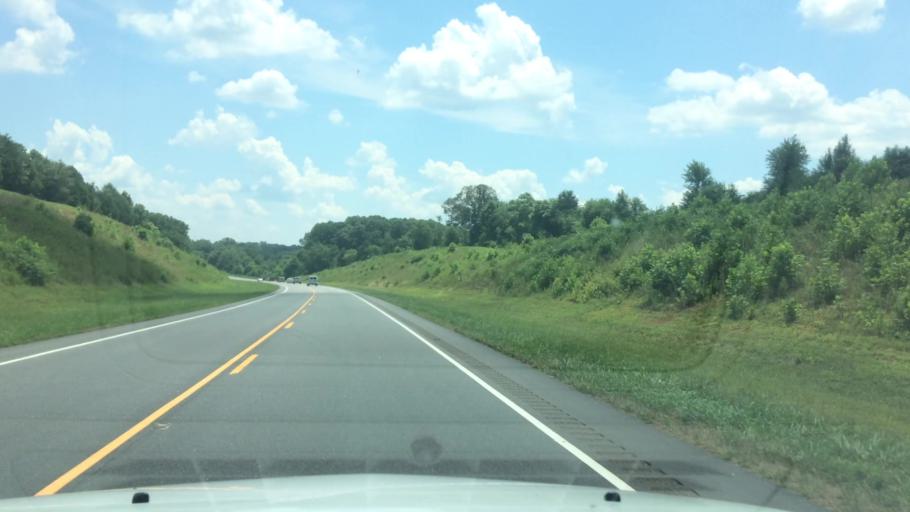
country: US
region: North Carolina
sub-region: Alexander County
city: Stony Point
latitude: 35.8664
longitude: -81.0617
